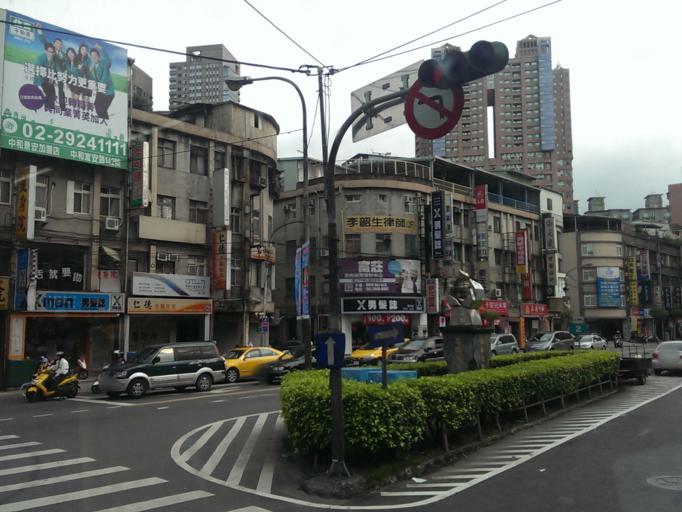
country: TW
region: Taipei
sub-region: Taipei
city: Banqiao
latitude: 24.9956
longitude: 121.5134
